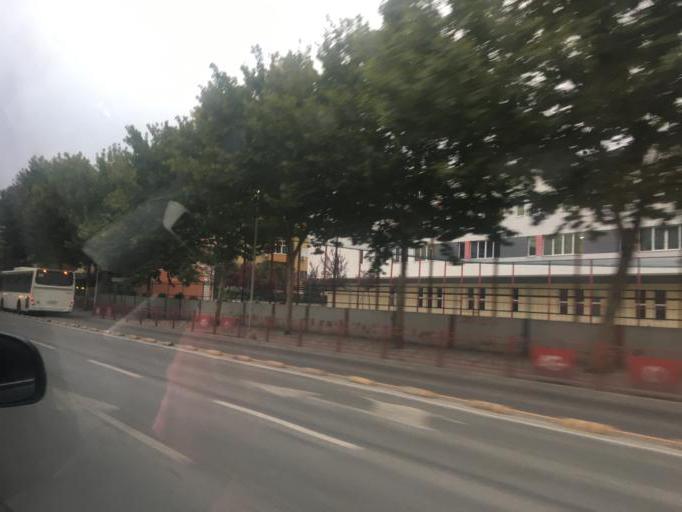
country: AL
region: Tirane
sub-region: Rrethi i Tiranes
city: Paskuqan
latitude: 41.3367
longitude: 19.7940
